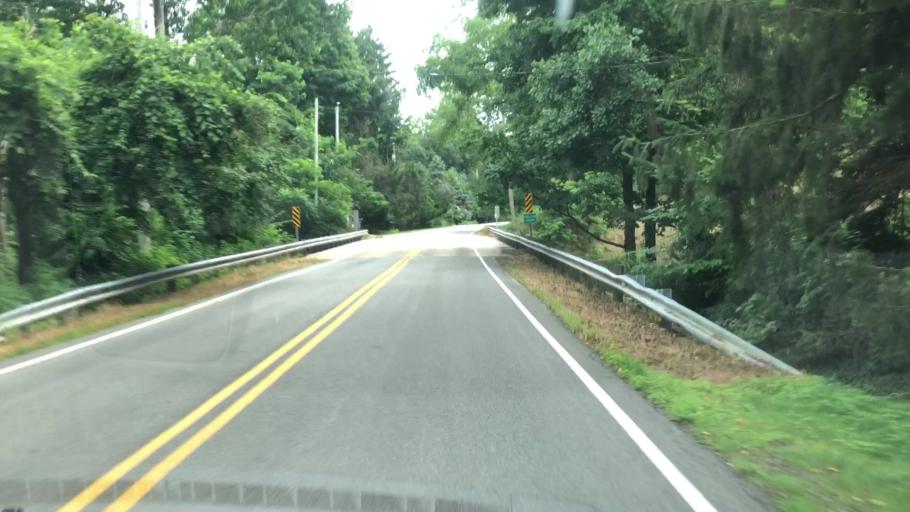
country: US
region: Ohio
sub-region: Summit County
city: Fairlawn
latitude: 41.1631
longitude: -81.5847
